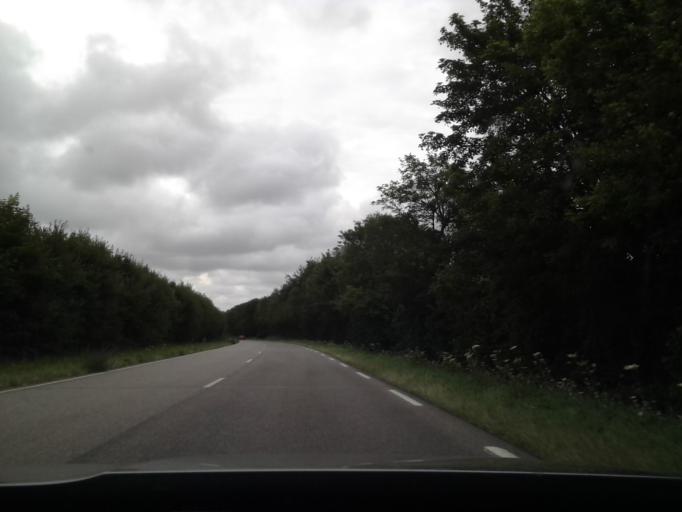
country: FR
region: Lower Normandy
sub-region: Departement du Calvados
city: Le Molay-Littry
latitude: 49.3335
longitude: -0.9161
